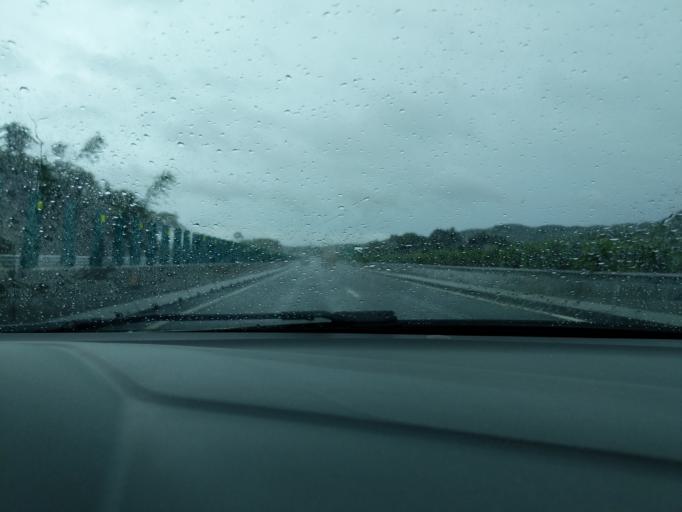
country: CN
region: Guangdong
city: Liangxi
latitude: 22.2650
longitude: 112.3204
